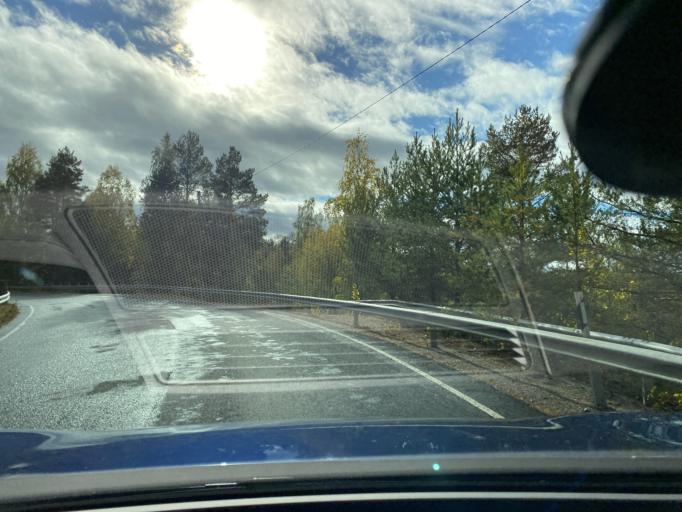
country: FI
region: Pirkanmaa
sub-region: Tampere
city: Nokia
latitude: 61.4785
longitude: 23.3395
